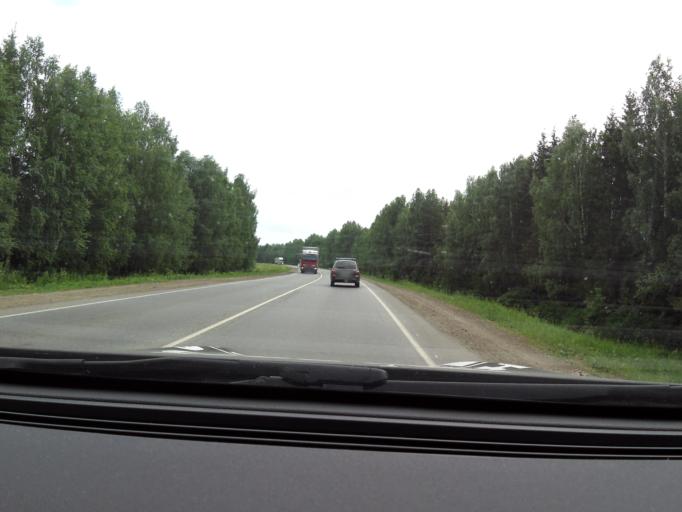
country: RU
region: Perm
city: Kukushtan
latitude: 57.4845
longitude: 56.6734
